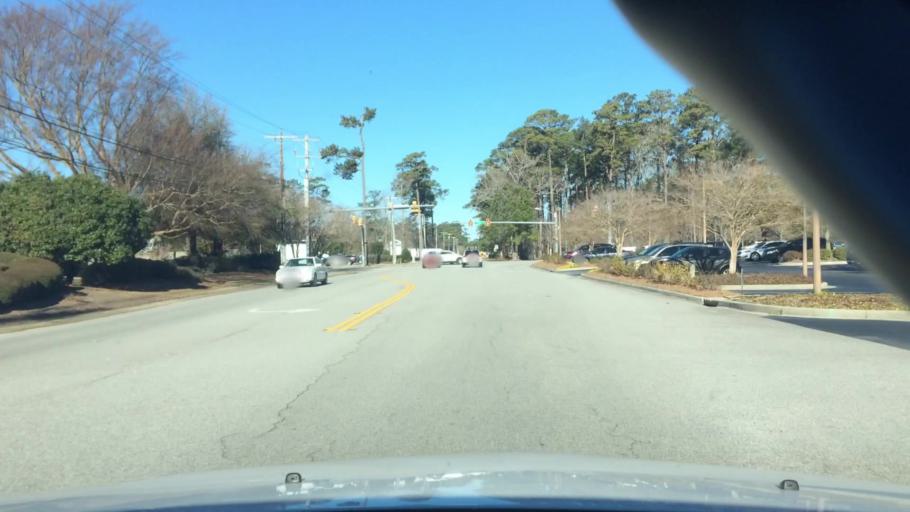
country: US
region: South Carolina
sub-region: Horry County
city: Myrtle Beach
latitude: 33.7299
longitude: -78.8560
